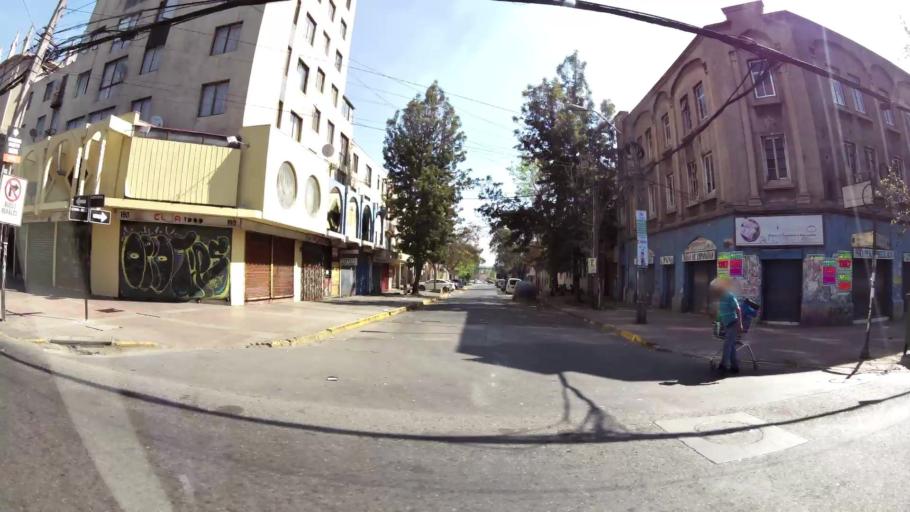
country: CL
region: Santiago Metropolitan
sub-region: Provincia de Santiago
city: Santiago
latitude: -33.4299
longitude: -70.6535
